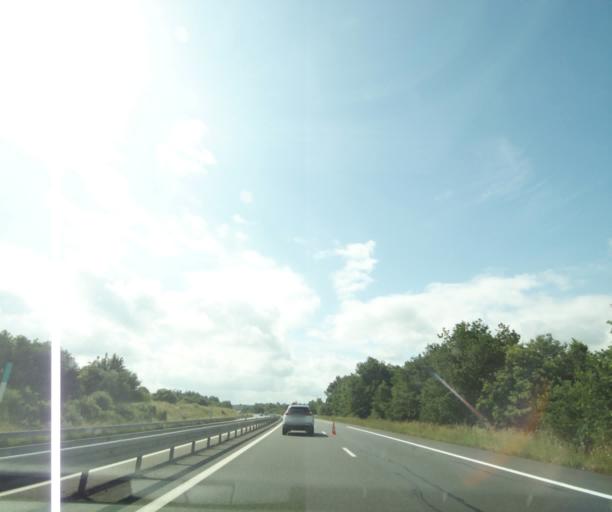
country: FR
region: Pays de la Loire
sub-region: Departement de Maine-et-Loire
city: Jumelles
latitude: 47.4012
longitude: -0.1188
